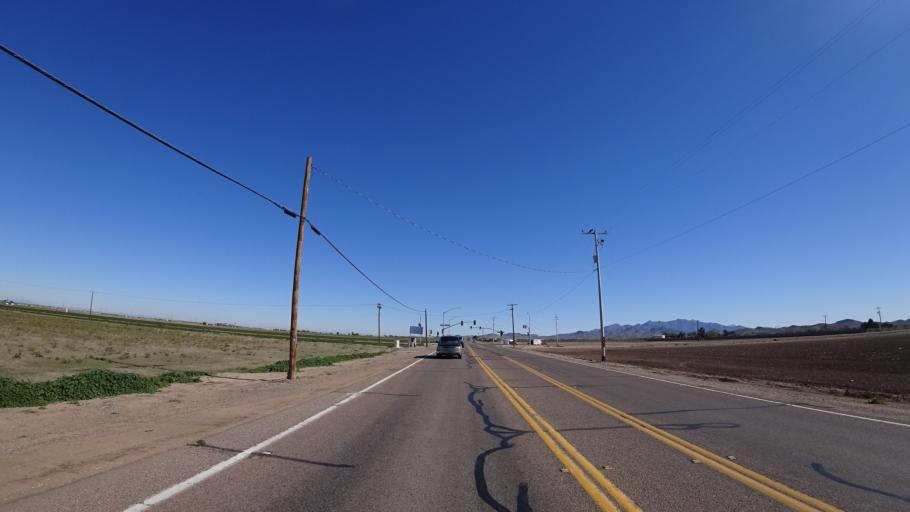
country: US
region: Arizona
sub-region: Maricopa County
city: Buckeye
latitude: 33.3776
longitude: -112.4789
